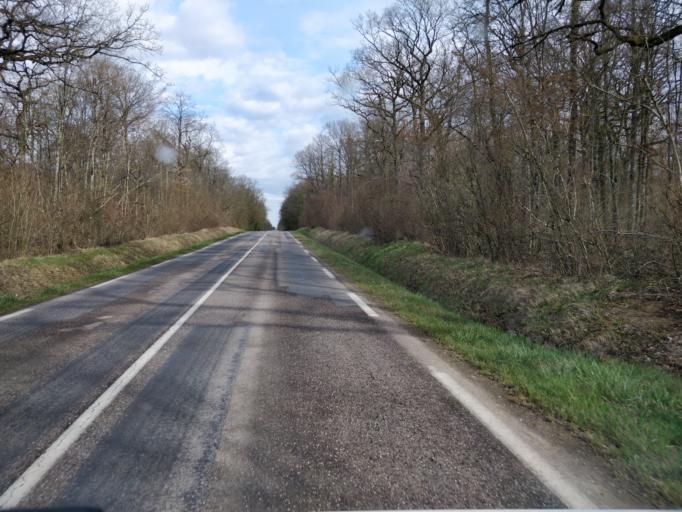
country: FR
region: Lorraine
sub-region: Departement de Meurthe-et-Moselle
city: Doncourt-les-Conflans
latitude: 49.0606
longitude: 5.8907
